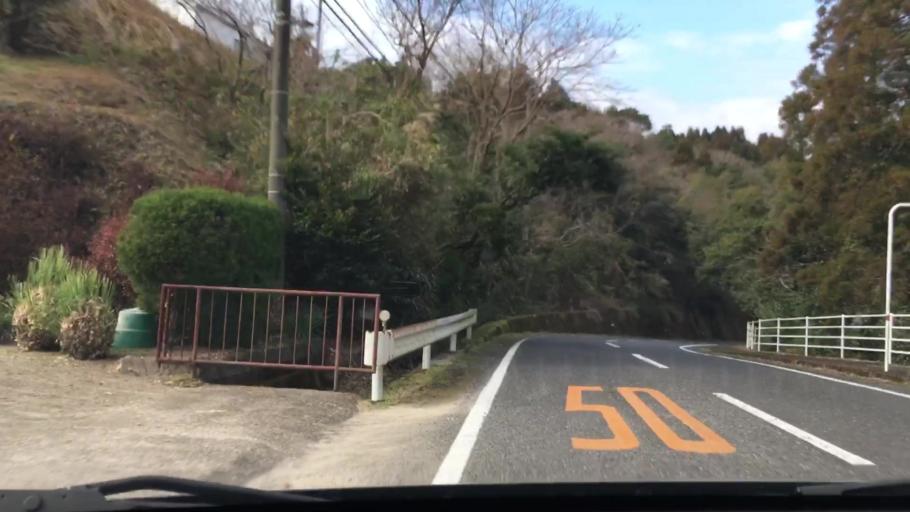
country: JP
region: Miyazaki
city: Kushima
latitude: 31.5417
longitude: 131.2422
